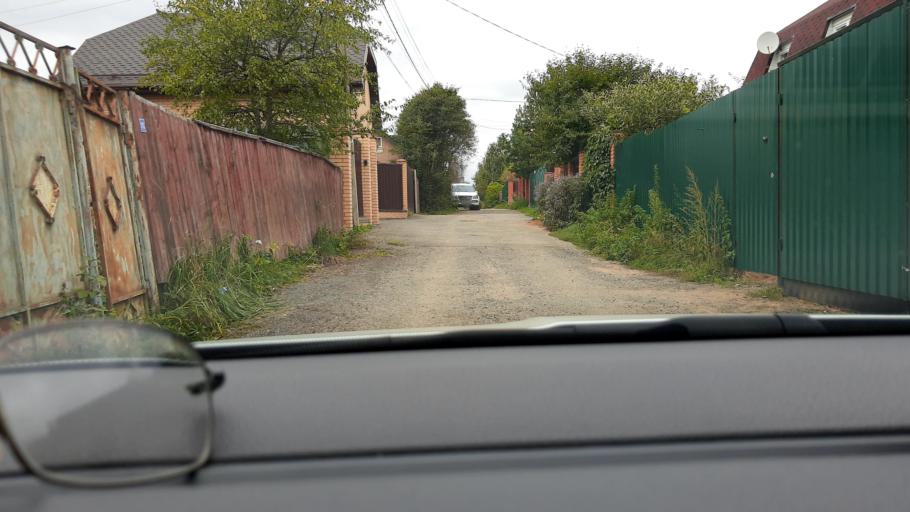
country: RU
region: Moskovskaya
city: Kokoshkino
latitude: 55.5914
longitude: 37.1929
